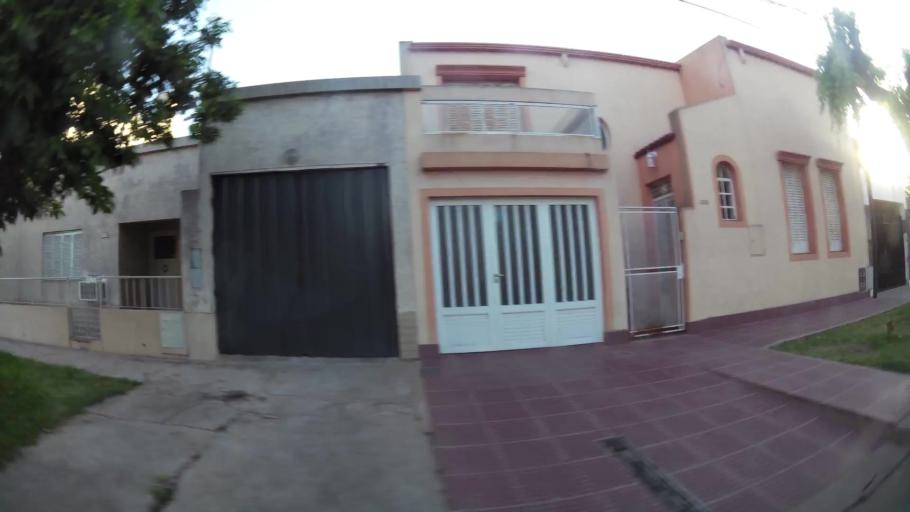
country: AR
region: Santa Fe
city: Santa Fe de la Vera Cruz
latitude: -31.6028
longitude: -60.6894
